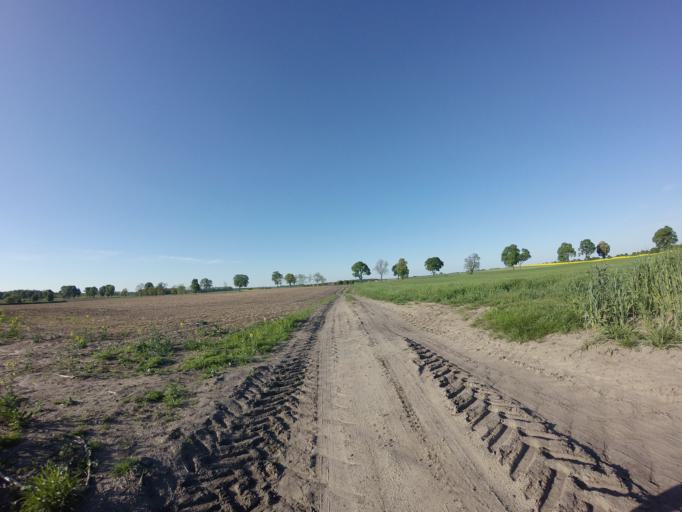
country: PL
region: West Pomeranian Voivodeship
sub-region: Powiat choszczenski
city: Choszczno
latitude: 53.1335
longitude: 15.3618
